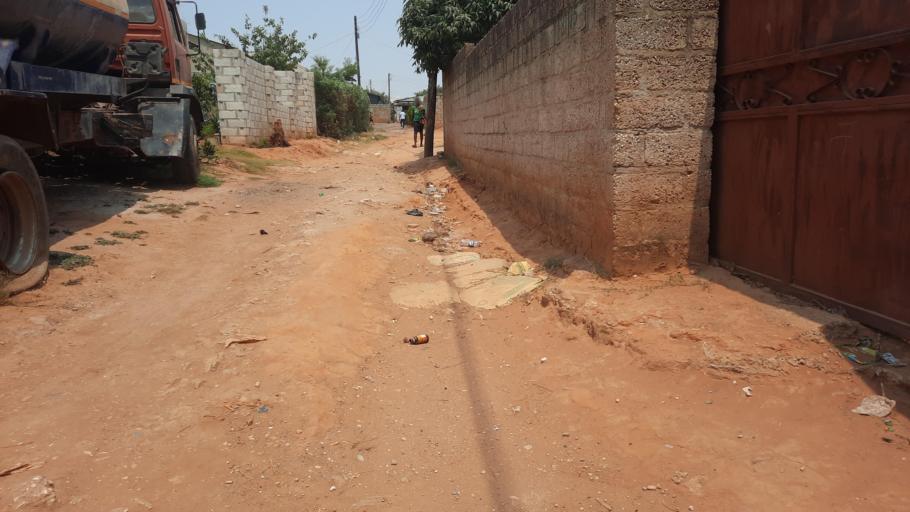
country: ZM
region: Lusaka
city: Lusaka
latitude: -15.3991
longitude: 28.3806
